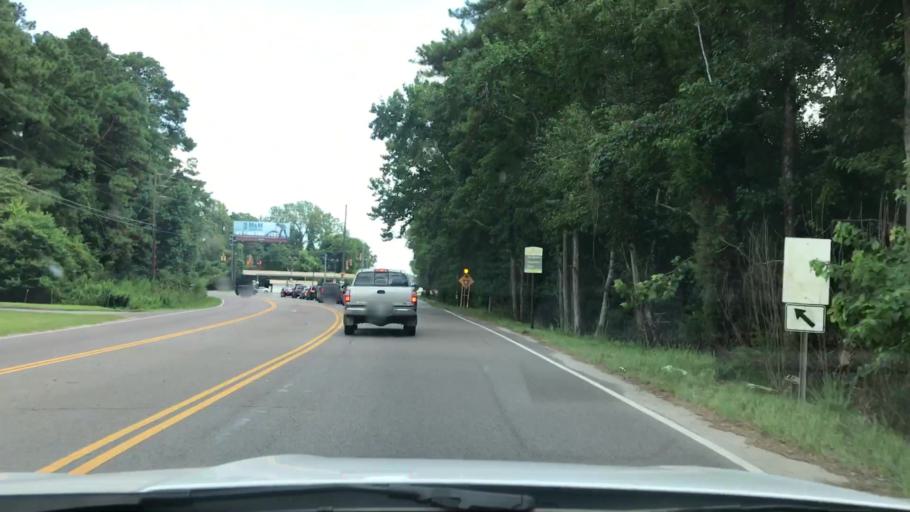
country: US
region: South Carolina
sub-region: Dorchester County
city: Summerville
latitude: 33.0343
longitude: -80.2001
